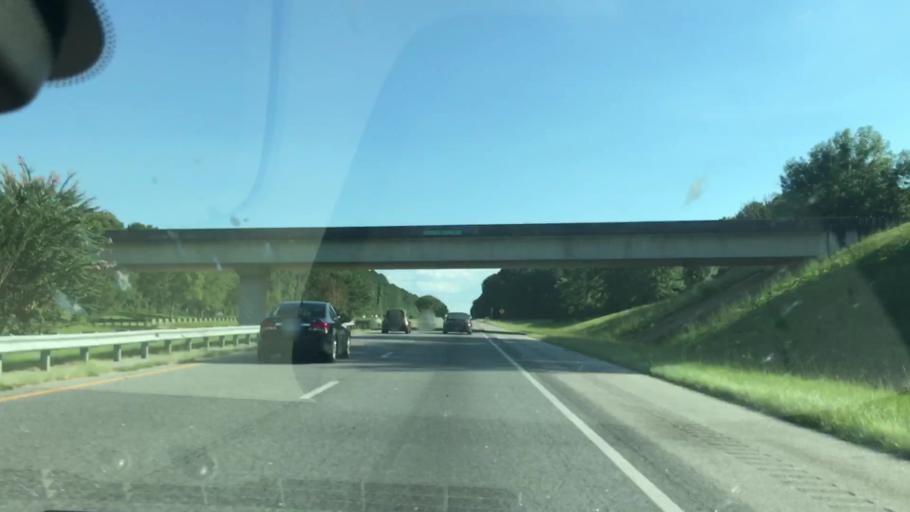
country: US
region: Georgia
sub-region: Harris County
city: Hamilton
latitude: 32.8141
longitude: -85.0213
